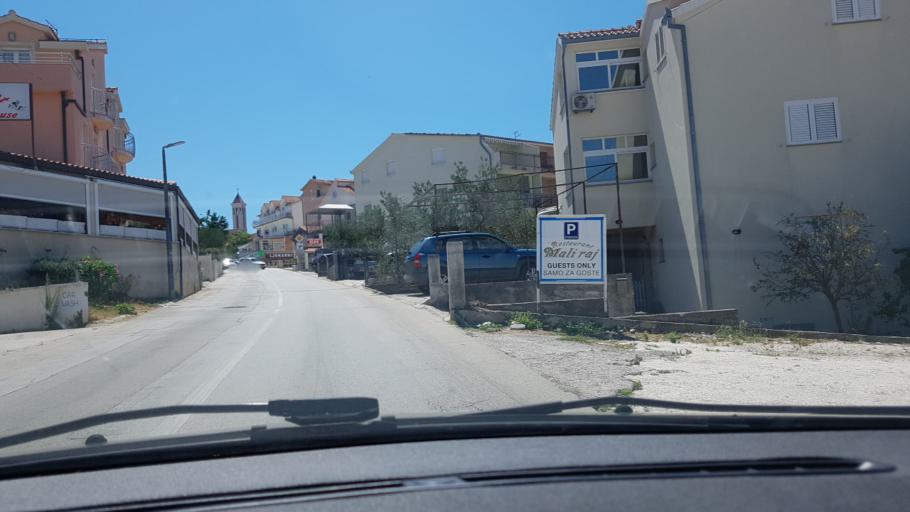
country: HR
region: Splitsko-Dalmatinska
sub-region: Grad Trogir
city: Trogir
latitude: 43.4947
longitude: 16.2634
